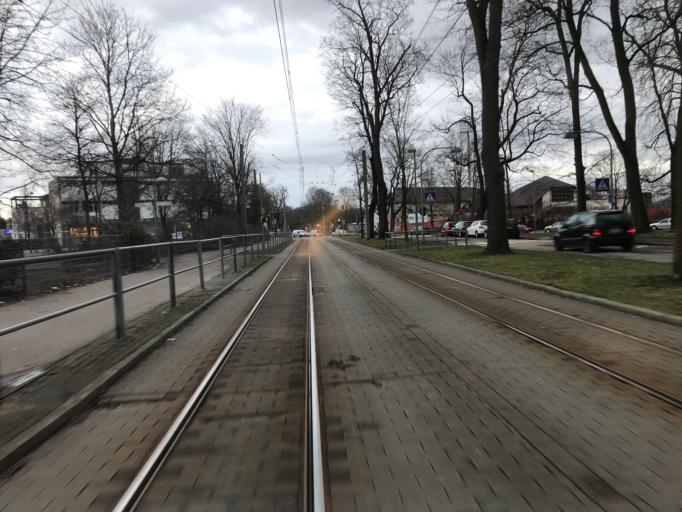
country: DE
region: Bavaria
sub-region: Swabia
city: Neu-Ulm
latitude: 48.4037
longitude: 10.0048
